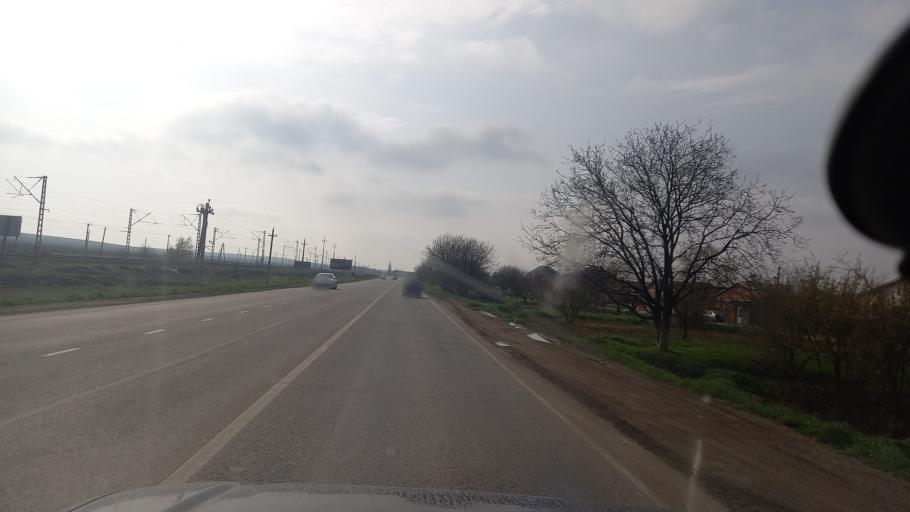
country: RU
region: Krasnodarskiy
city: Varenikovskaya
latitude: 45.1126
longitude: 37.6294
